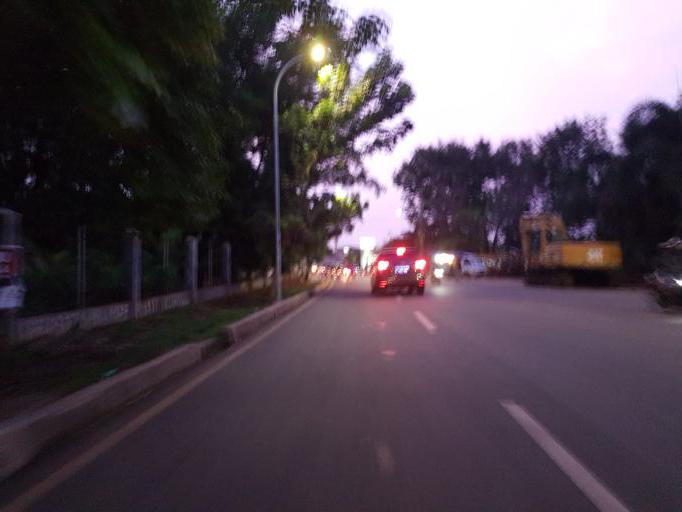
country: ID
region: West Java
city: Serpong
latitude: -6.3270
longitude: 106.6718
